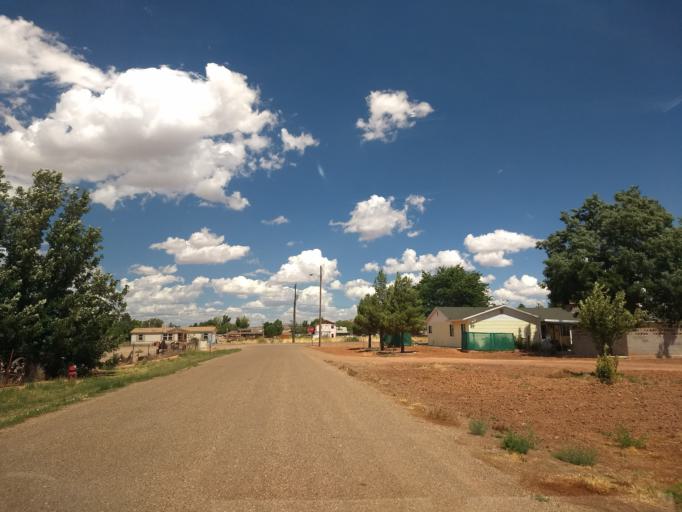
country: US
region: Arizona
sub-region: Coconino County
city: Fredonia
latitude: 36.9449
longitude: -112.5205
